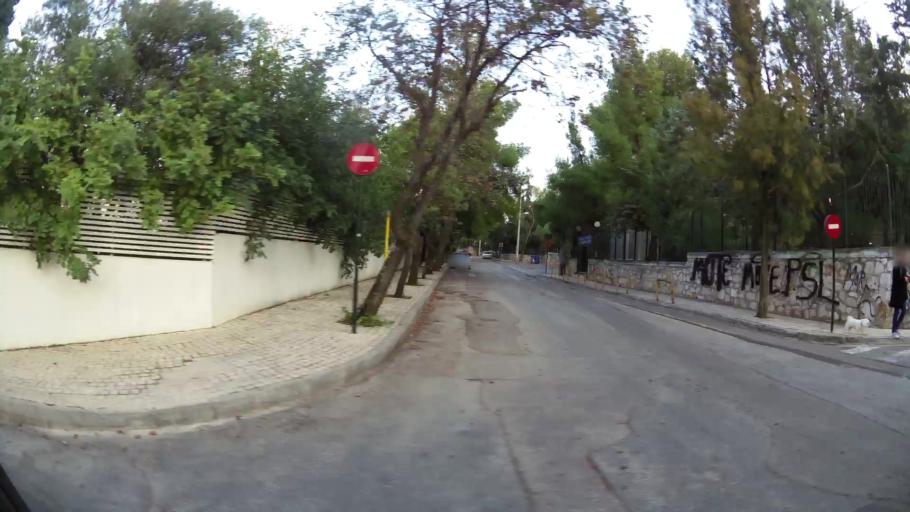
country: GR
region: Attica
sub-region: Nomarchia Athinas
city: Psychiko
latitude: 38.0181
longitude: 23.7763
